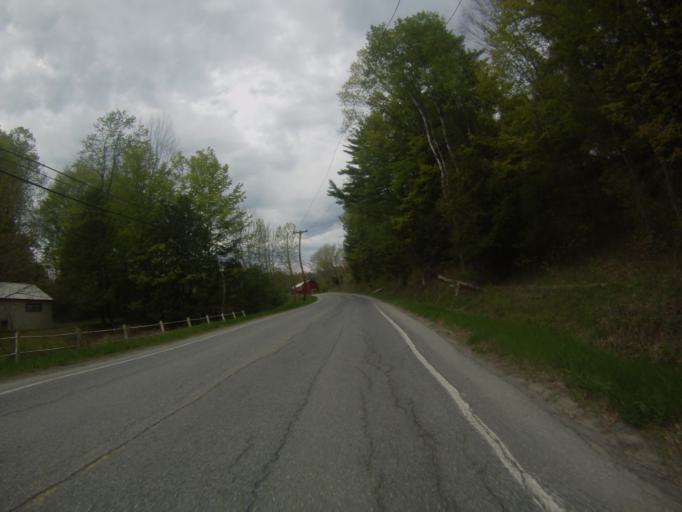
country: US
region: New York
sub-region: Essex County
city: Port Henry
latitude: 43.9484
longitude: -73.4733
